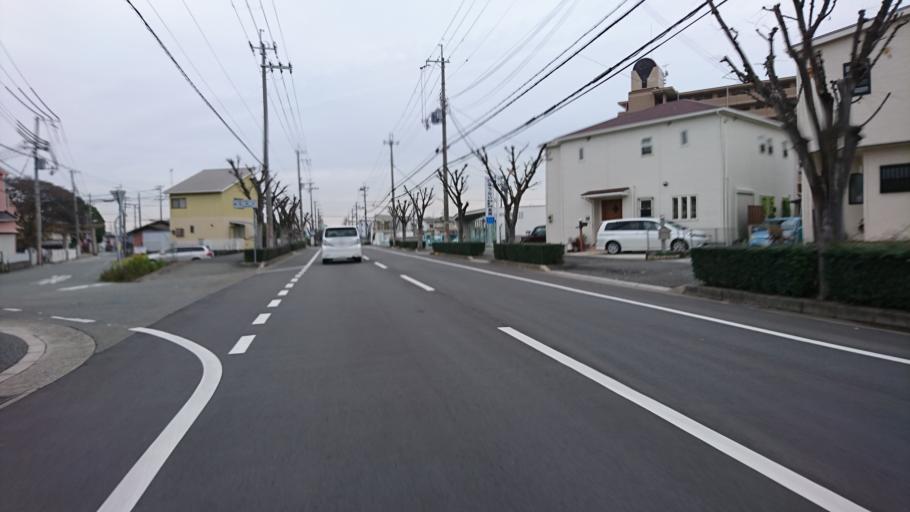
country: JP
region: Hyogo
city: Kakogawacho-honmachi
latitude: 34.7645
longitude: 134.8220
